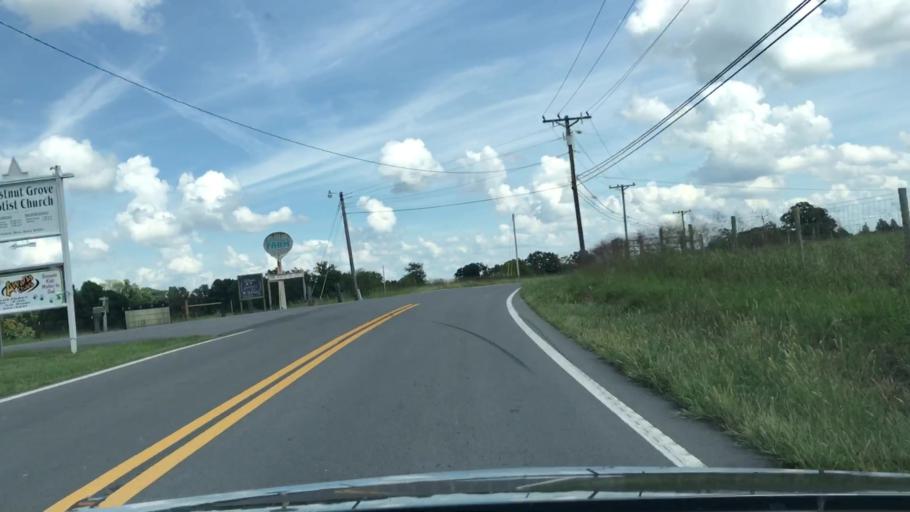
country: US
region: Tennessee
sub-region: Sumner County
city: Portland
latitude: 36.5339
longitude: -86.5355
